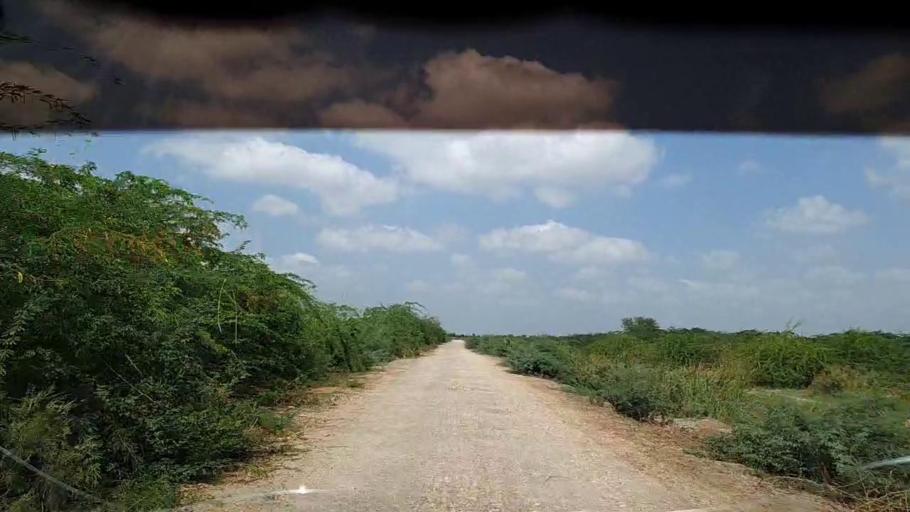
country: PK
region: Sindh
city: Kadhan
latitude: 24.5860
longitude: 68.9697
